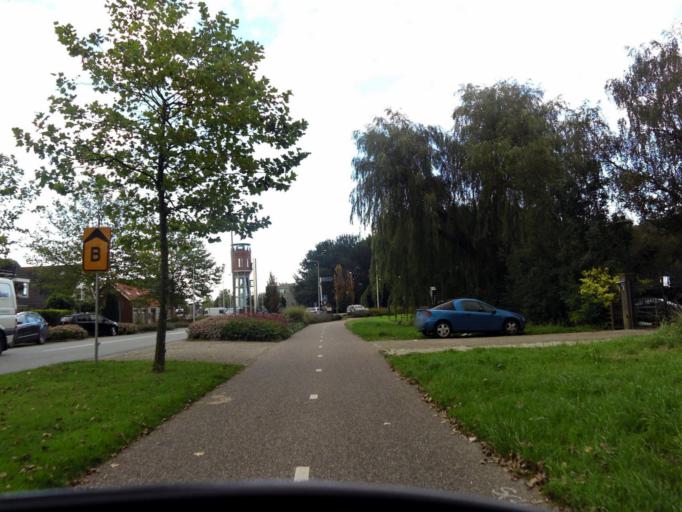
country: NL
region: South Holland
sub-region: Gemeente Leiderdorp
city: Leiderdorp
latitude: 52.1278
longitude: 4.5814
